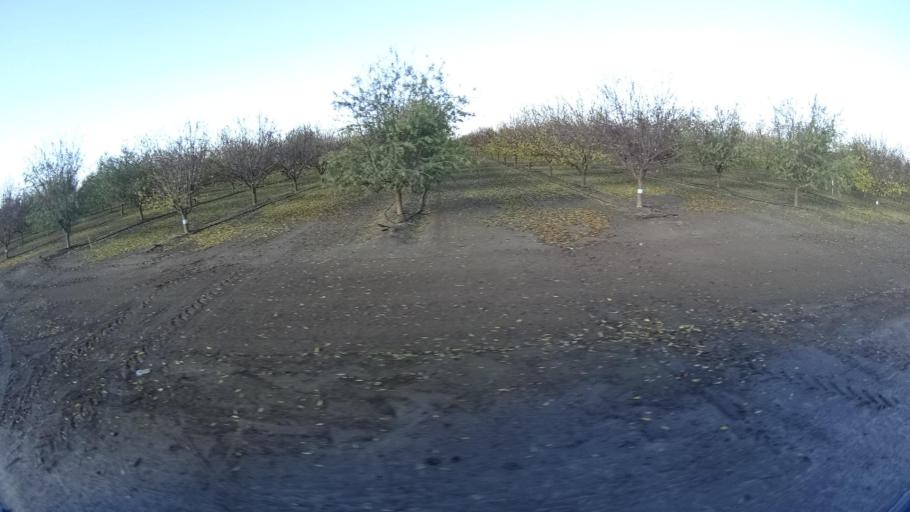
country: US
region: California
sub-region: Kern County
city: Delano
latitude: 35.7414
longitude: -119.3301
